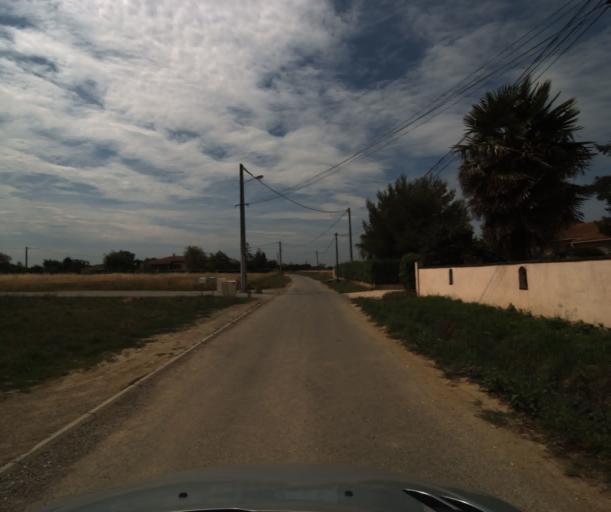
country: FR
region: Midi-Pyrenees
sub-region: Departement de la Haute-Garonne
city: Lacasse
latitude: 43.4159
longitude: 1.2778
